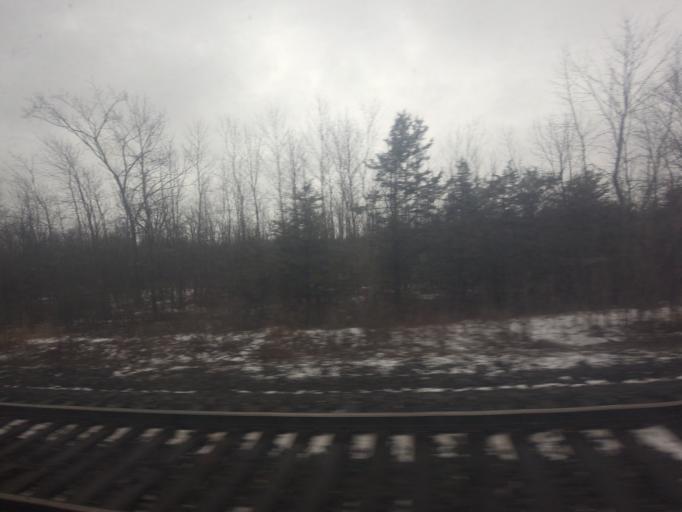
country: CA
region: Ontario
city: Belleville
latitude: 44.2034
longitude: -77.2551
